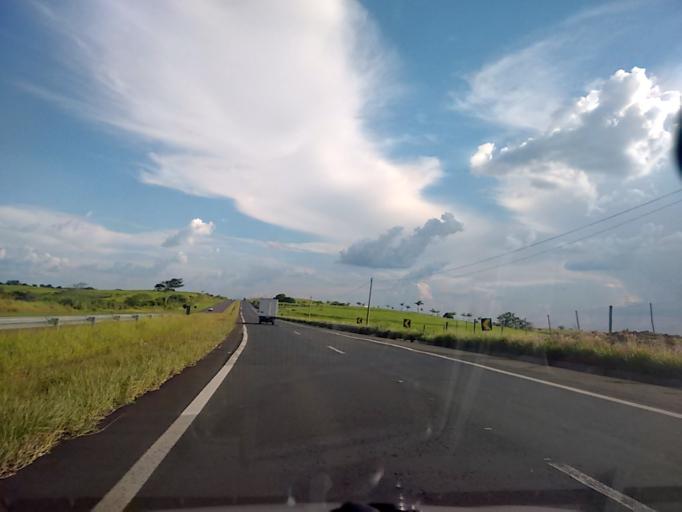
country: BR
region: Sao Paulo
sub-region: Duartina
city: Duartina
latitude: -22.2951
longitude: -49.4966
